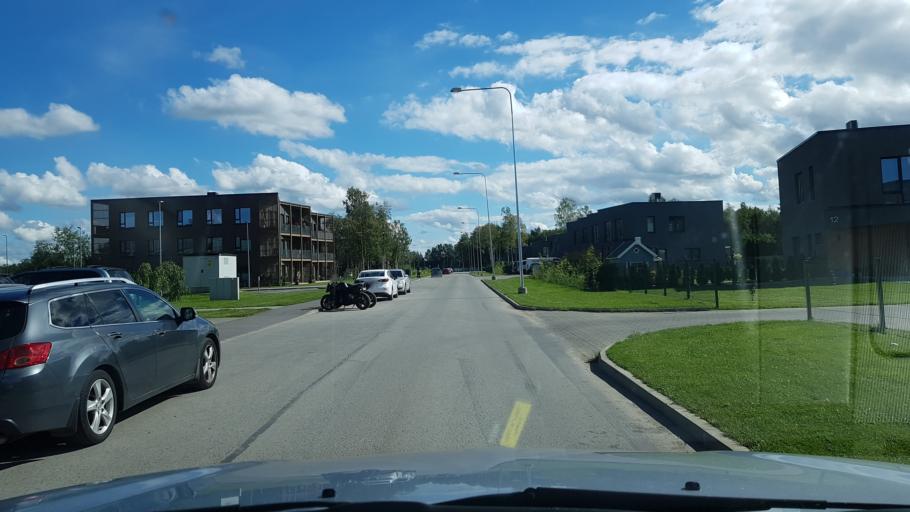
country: EE
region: Harju
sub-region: Tallinna linn
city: Tallinn
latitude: 59.4010
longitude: 24.7925
